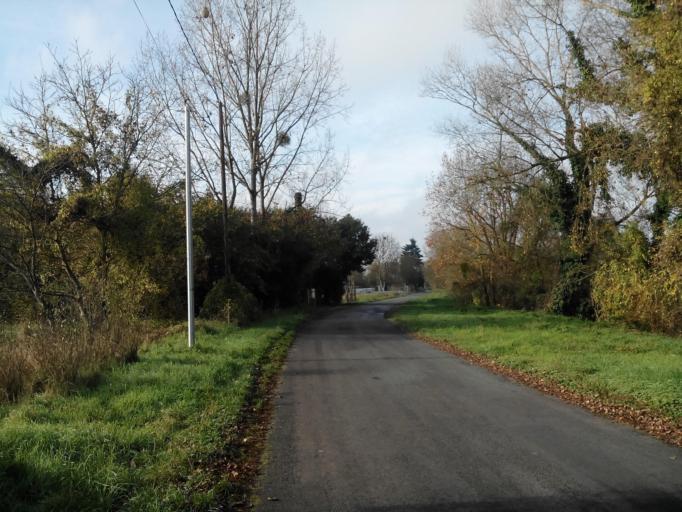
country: FR
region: Centre
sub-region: Departement d'Indre-et-Loire
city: Saint-Cyr-sur-Loire
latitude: 47.3858
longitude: 0.6321
